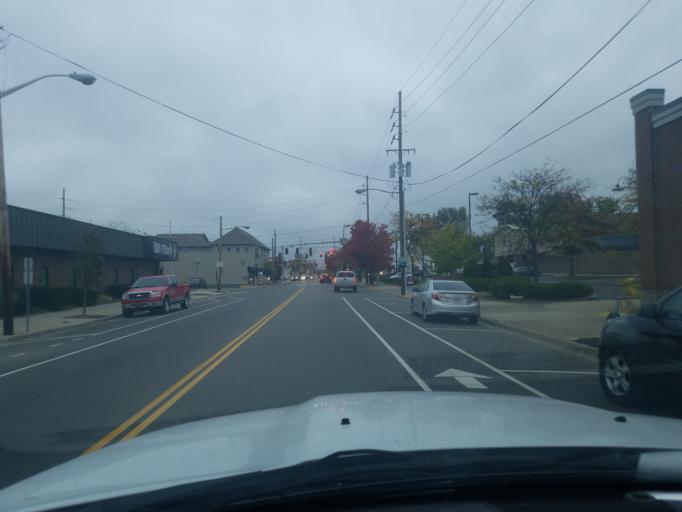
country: US
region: Indiana
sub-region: Floyd County
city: New Albany
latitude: 38.2917
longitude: -85.8063
